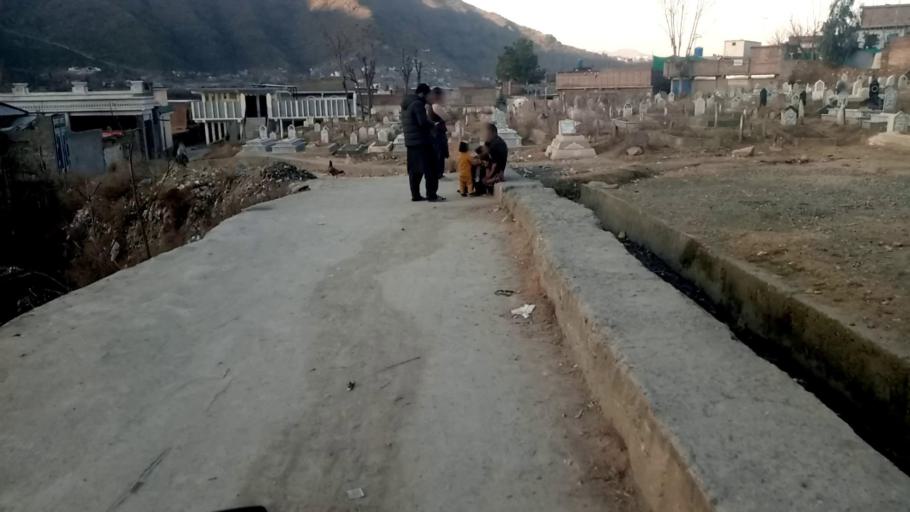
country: PK
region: Khyber Pakhtunkhwa
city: Saidu Sharif
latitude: 34.7383
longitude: 72.3435
